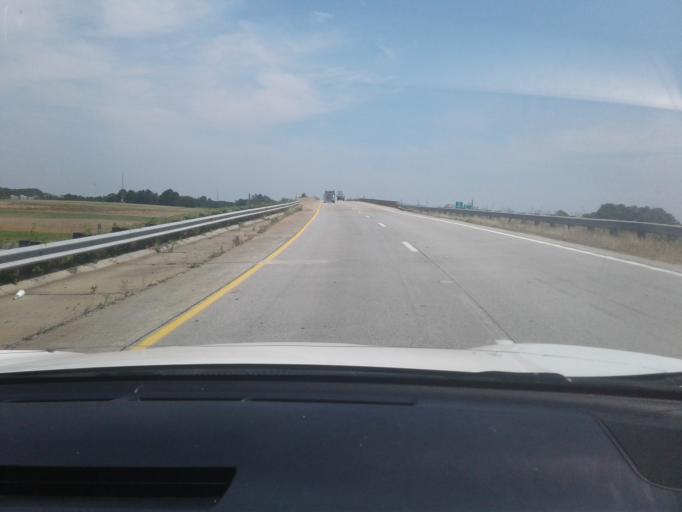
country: US
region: North Carolina
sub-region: Johnston County
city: Benson
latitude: 35.3879
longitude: -78.5198
